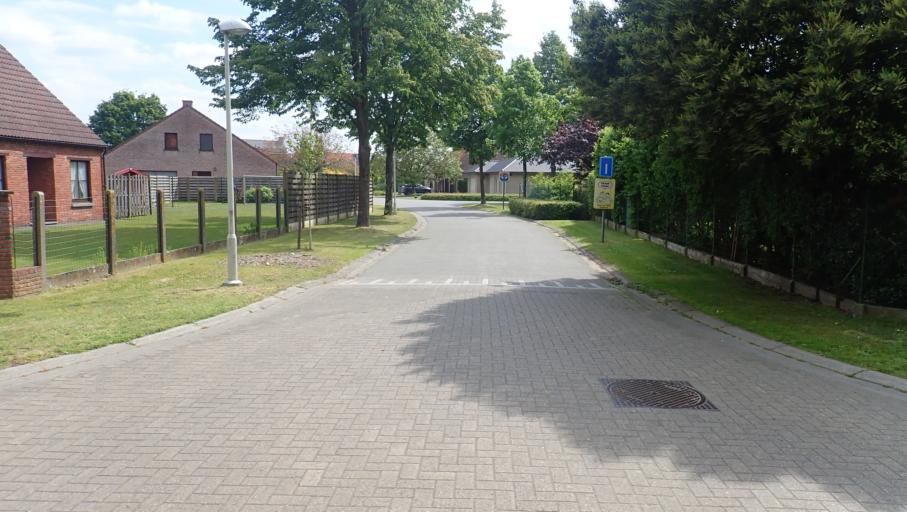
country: BE
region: Flanders
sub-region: Provincie Antwerpen
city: Zoersel
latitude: 51.2991
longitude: 4.6788
